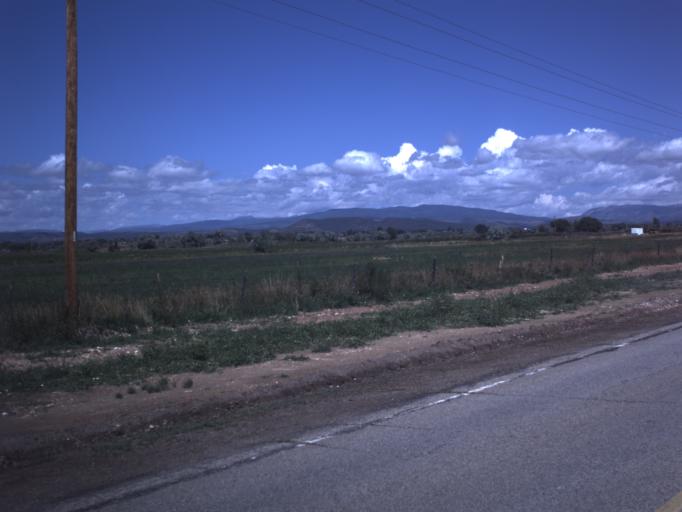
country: US
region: Utah
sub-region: Duchesne County
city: Roosevelt
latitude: 40.4187
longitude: -110.0299
